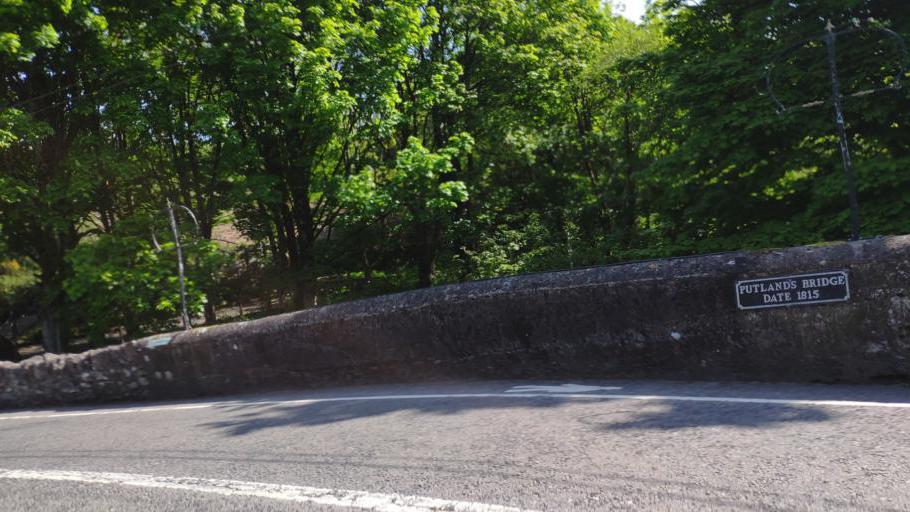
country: IE
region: Munster
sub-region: County Cork
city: Blarney
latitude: 51.9540
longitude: -8.5740
